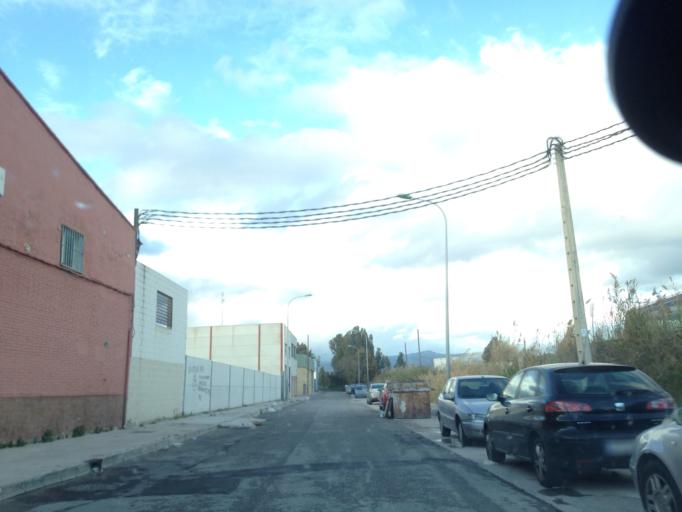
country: ES
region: Andalusia
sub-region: Provincia de Malaga
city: Torremolinos
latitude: 36.6715
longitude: -4.4697
